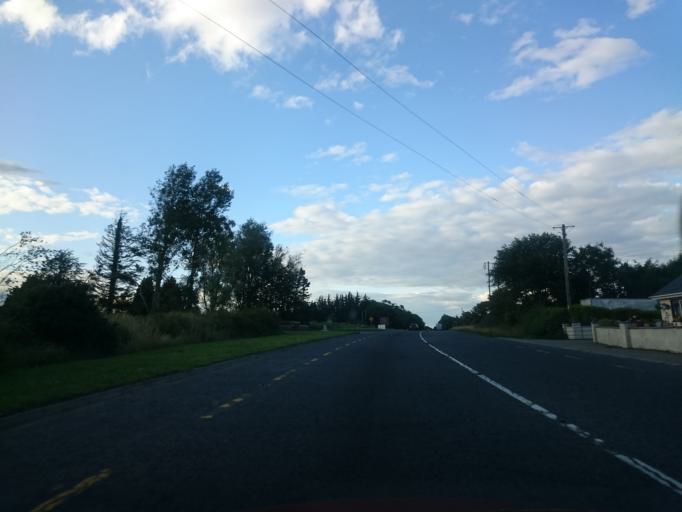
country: IE
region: Leinster
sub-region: Loch Garman
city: Loch Garman
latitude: 52.2929
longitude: -6.4627
